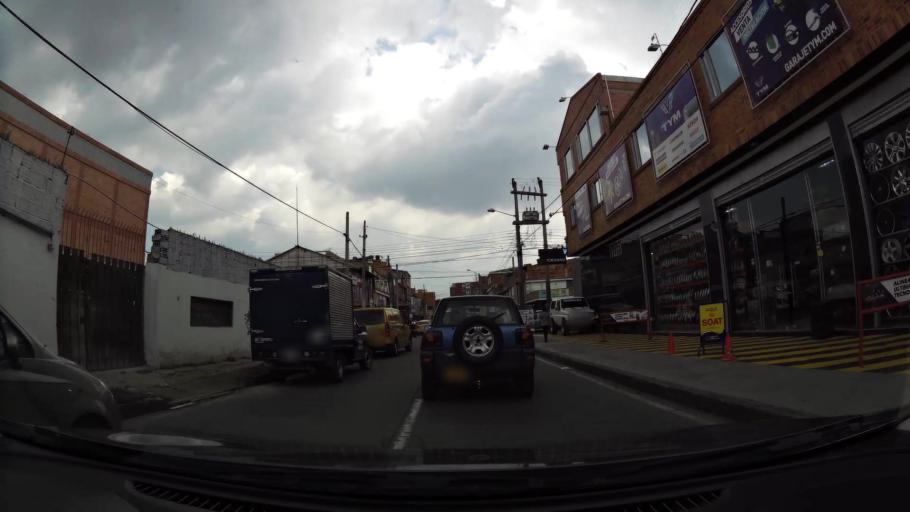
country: CO
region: Bogota D.C.
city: Barrio San Luis
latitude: 4.7429
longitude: -74.0453
